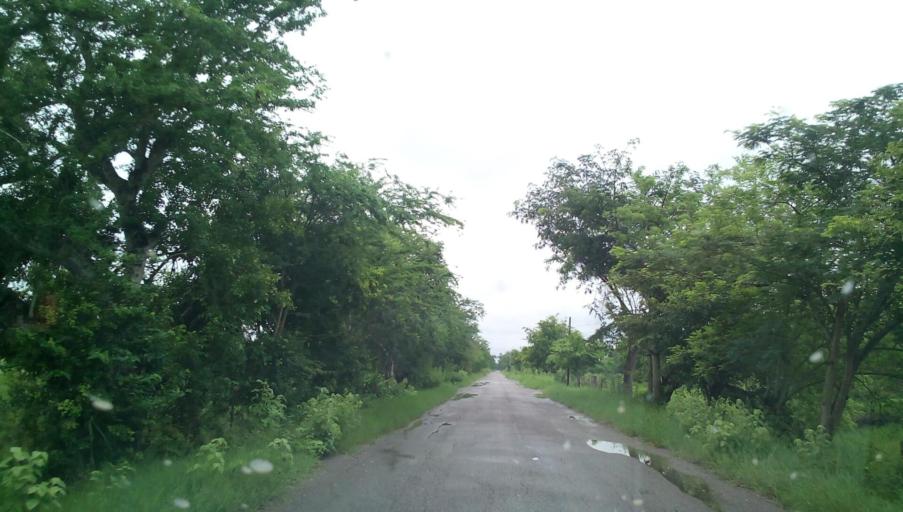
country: MX
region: Veracruz
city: Tempoal de Sanchez
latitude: 21.4725
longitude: -98.4202
